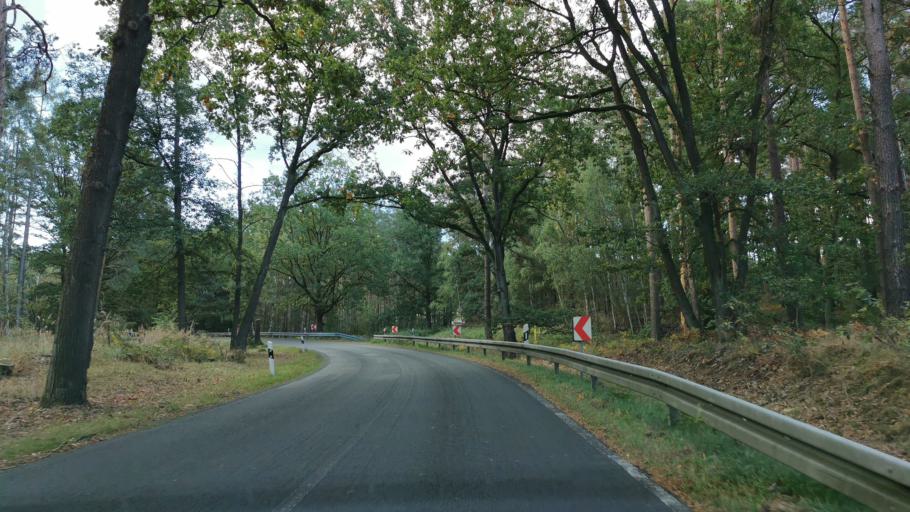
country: DE
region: Brandenburg
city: Fichtenwalde
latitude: 52.2986
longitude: 12.9449
